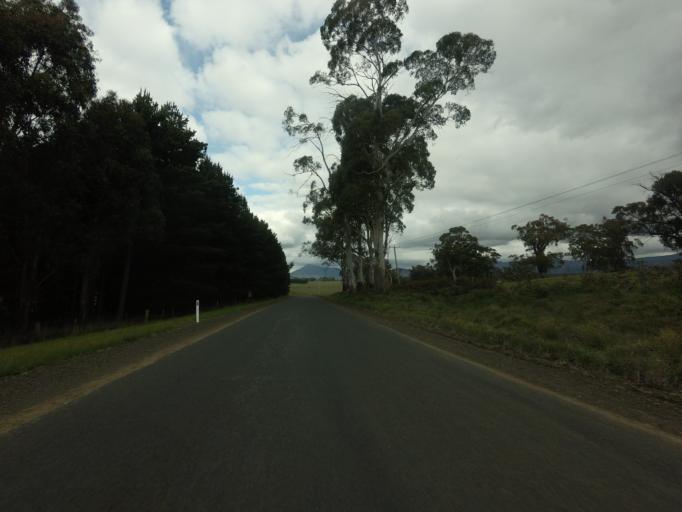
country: AU
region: Tasmania
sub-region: Northern Midlands
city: Longford
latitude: -41.7673
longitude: 147.0860
